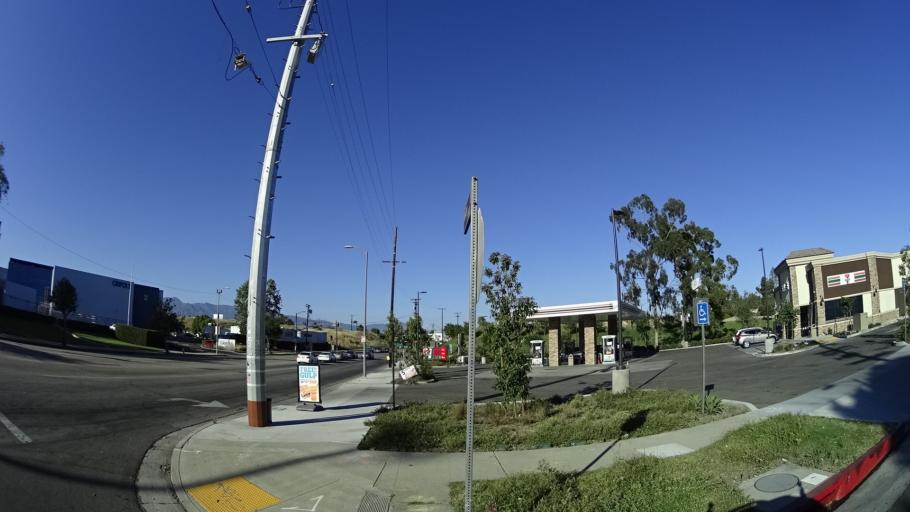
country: US
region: California
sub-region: Los Angeles County
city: Belvedere
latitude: 34.0741
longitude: -118.1626
